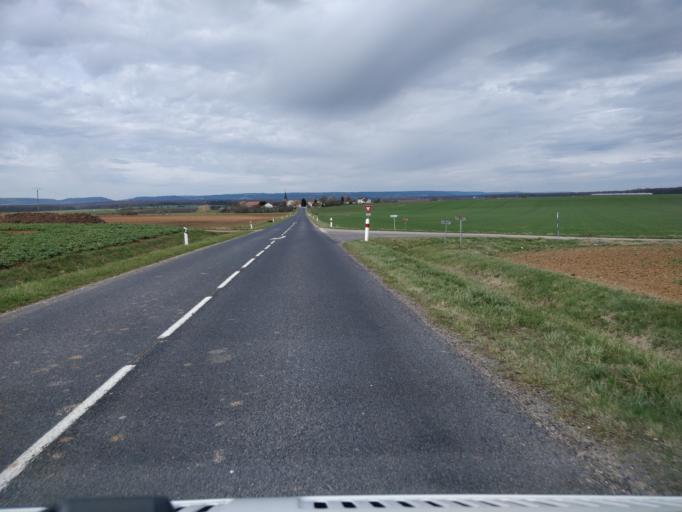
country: FR
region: Lorraine
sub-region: Departement de la Meuse
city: Vigneulles-les-Hattonchatel
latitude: 48.9597
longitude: 5.8383
